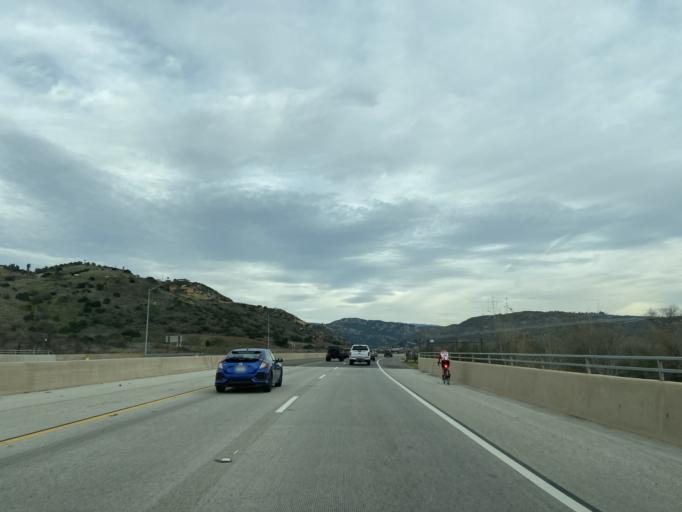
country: US
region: California
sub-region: San Diego County
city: Bonsall
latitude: 33.3143
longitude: -117.1944
